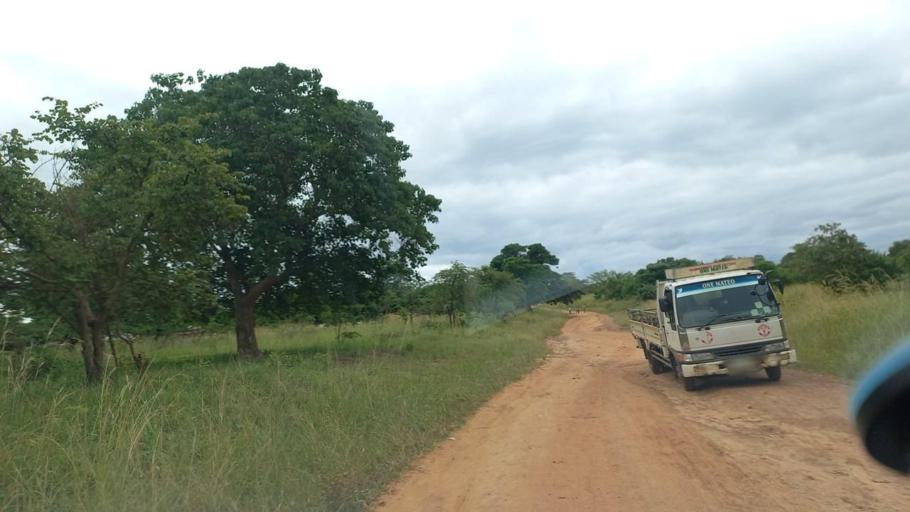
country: ZM
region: Lusaka
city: Chongwe
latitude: -15.4548
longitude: 28.8549
